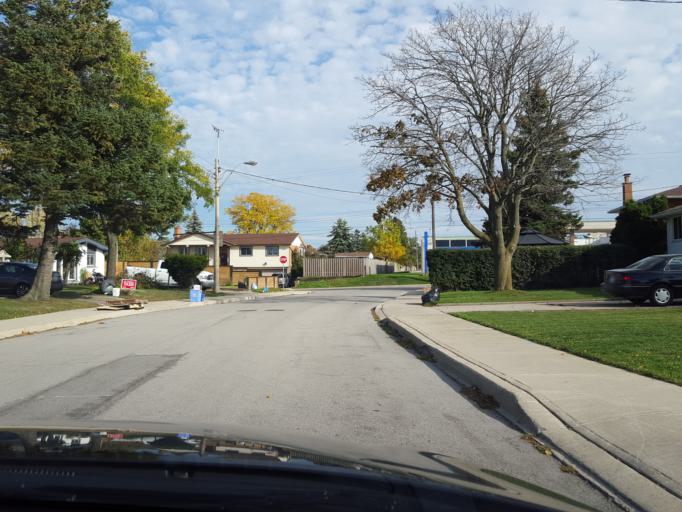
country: CA
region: Ontario
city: Hamilton
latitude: 43.2347
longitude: -79.9118
